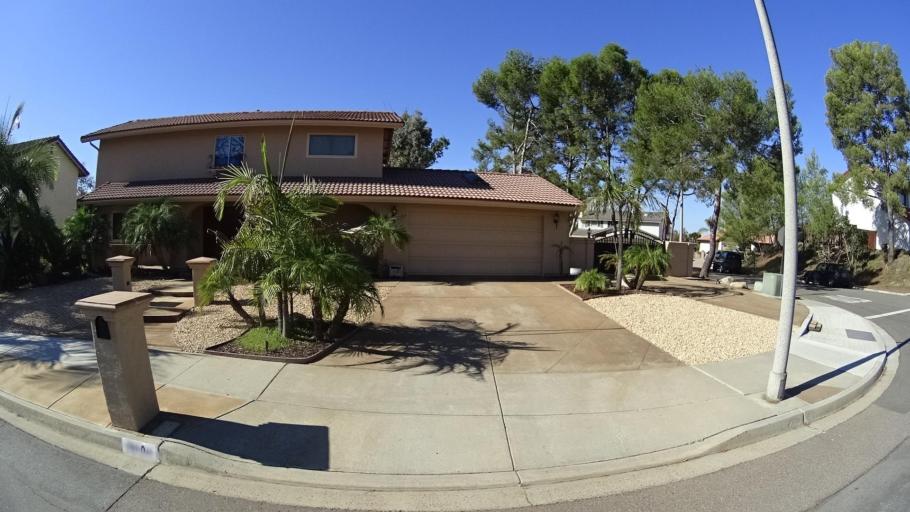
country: US
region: California
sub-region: San Diego County
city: Bonita
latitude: 32.6688
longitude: -117.0036
